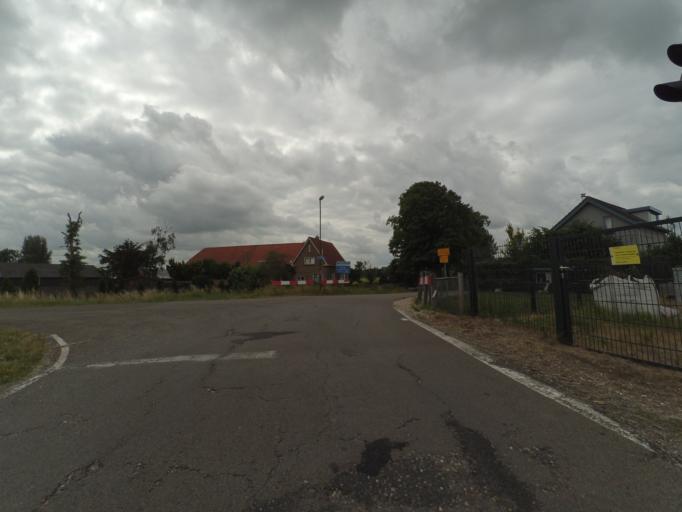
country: NL
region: South Holland
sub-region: Gemeente Leerdam
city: Leerdam
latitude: 51.8816
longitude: 5.0262
